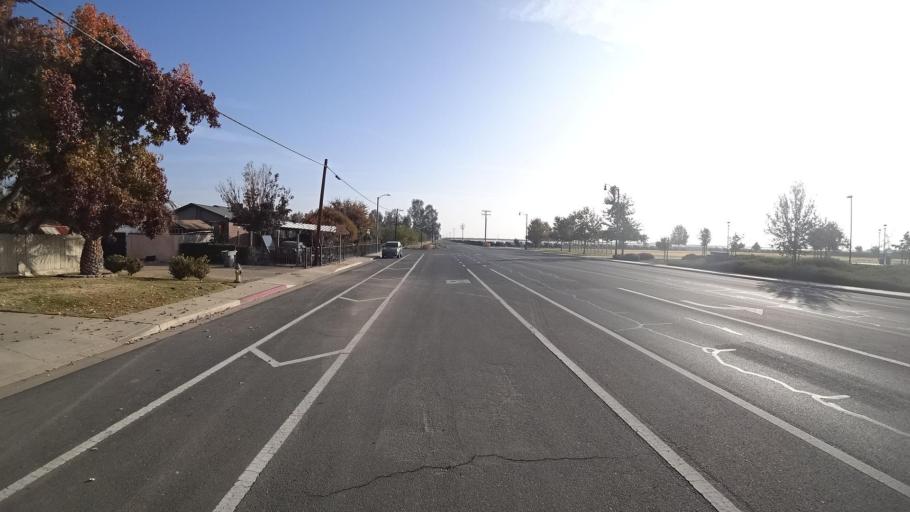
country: US
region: California
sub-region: Kern County
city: McFarland
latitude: 35.6745
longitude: -119.2182
